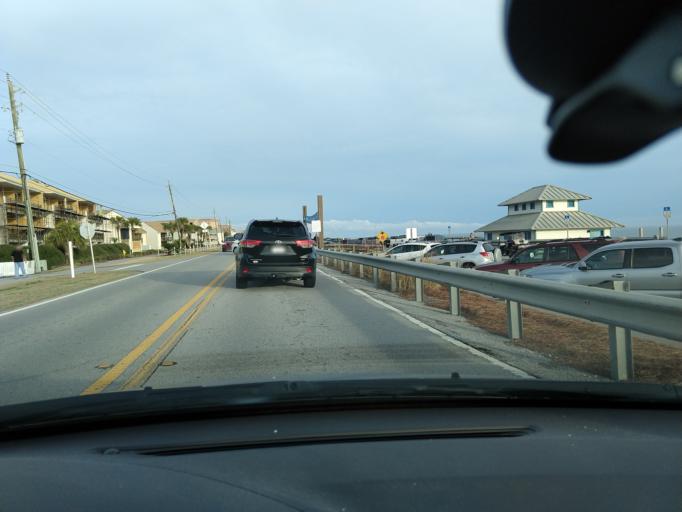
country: US
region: Florida
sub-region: Walton County
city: Miramar Beach
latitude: 30.3784
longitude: -86.3878
